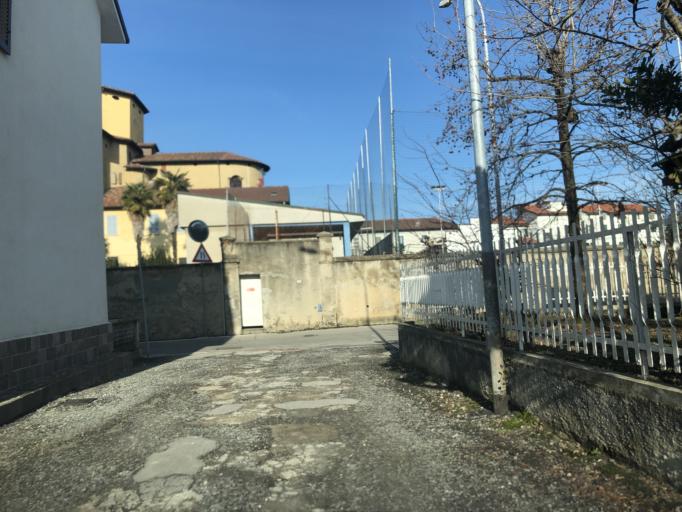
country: IT
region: Lombardy
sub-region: Provincia di Monza e Brianza
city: Sulbiate
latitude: 45.6335
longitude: 9.4221
